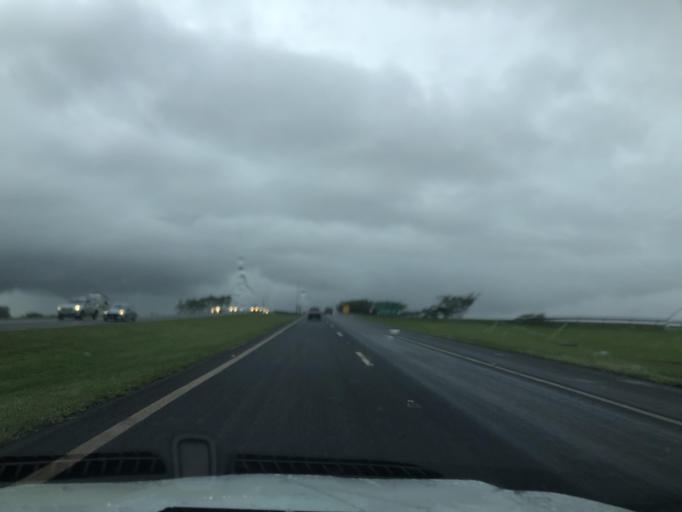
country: BR
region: Sao Paulo
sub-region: Jardinopolis
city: Jardinopolis
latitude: -21.0912
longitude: -47.7958
